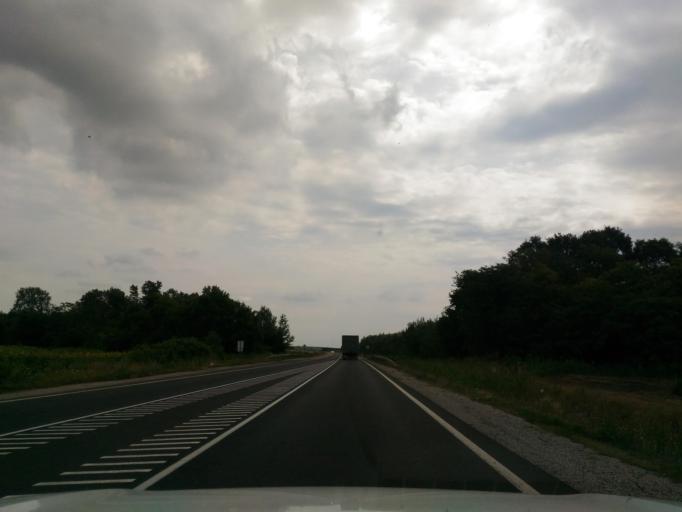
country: HU
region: Pest
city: Tortel
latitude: 47.1926
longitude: 19.9216
